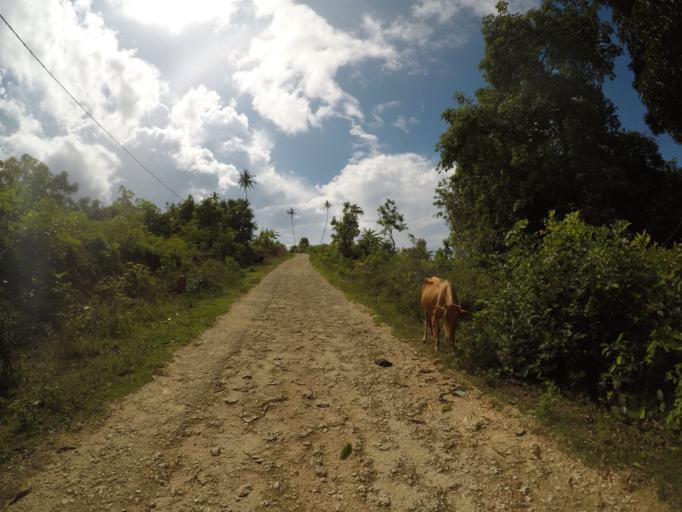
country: TZ
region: Pemba South
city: Mtambile
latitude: -5.3487
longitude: 39.6939
